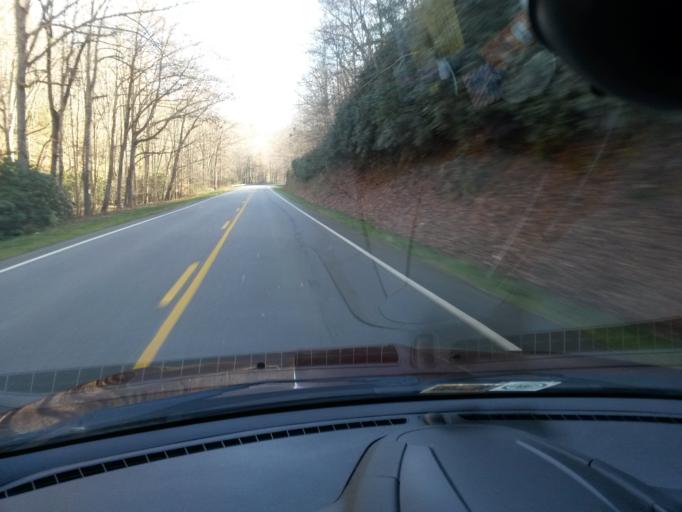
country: US
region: Virginia
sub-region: Henry County
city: Pannill Fork
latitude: 36.7729
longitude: -80.1116
